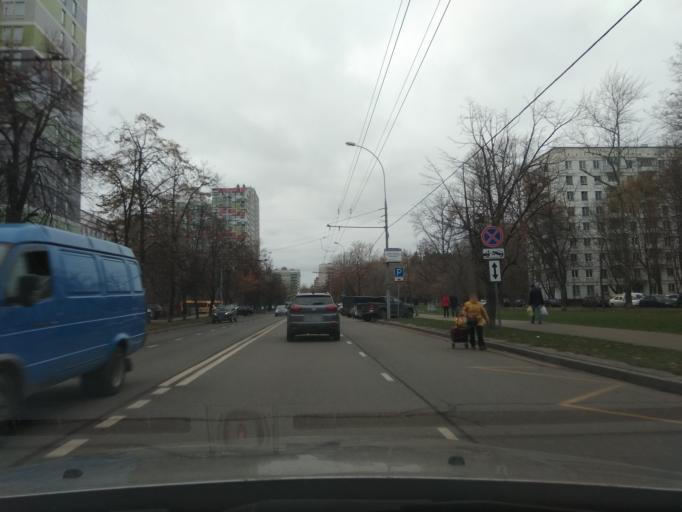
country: RU
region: Moskovskaya
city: Khoroshevo-Mnevniki
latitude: 55.7846
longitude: 37.4698
